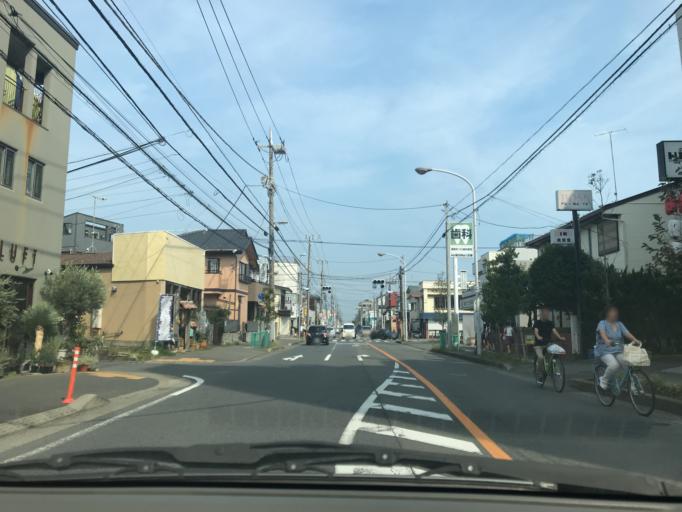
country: JP
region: Kanagawa
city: Chigasaki
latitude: 35.3250
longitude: 139.4138
